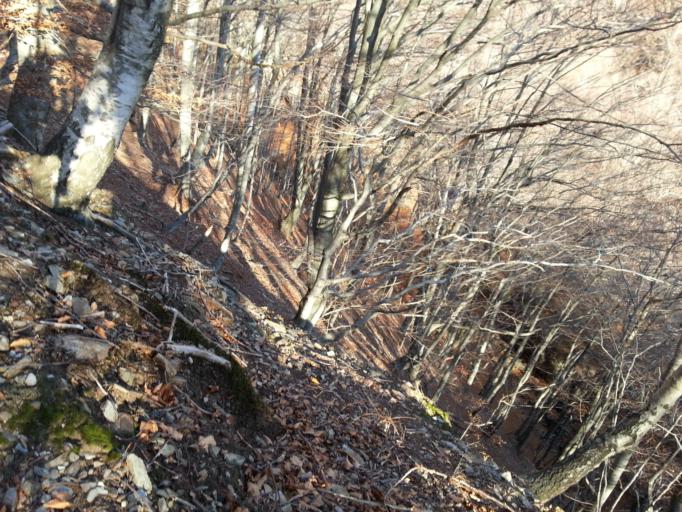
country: CH
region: Ticino
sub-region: Lugano District
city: Gravesano
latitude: 46.0563
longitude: 8.8671
